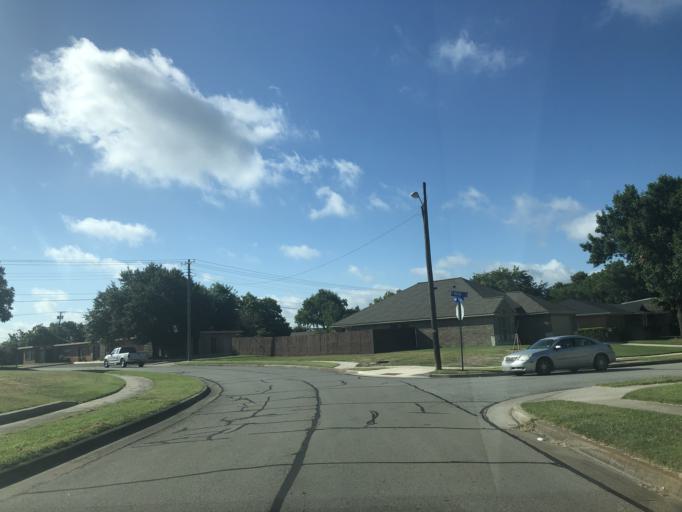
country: US
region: Texas
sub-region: Dallas County
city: Duncanville
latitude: 32.6593
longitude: -96.9090
